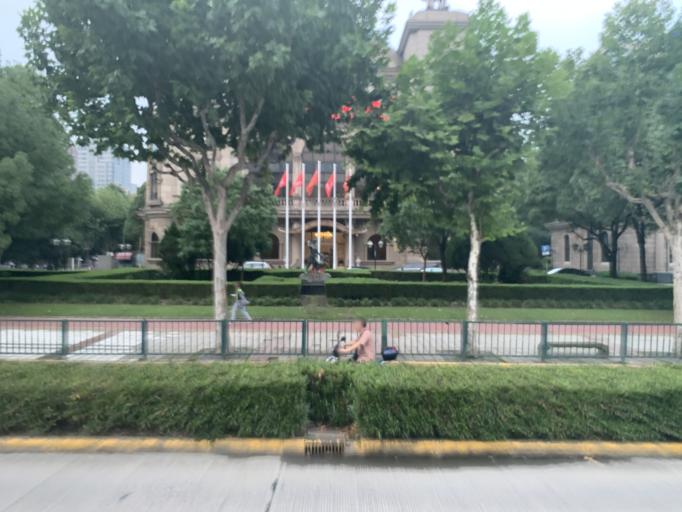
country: CN
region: Shanghai Shi
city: Pudong
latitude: 31.2403
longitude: 121.5266
